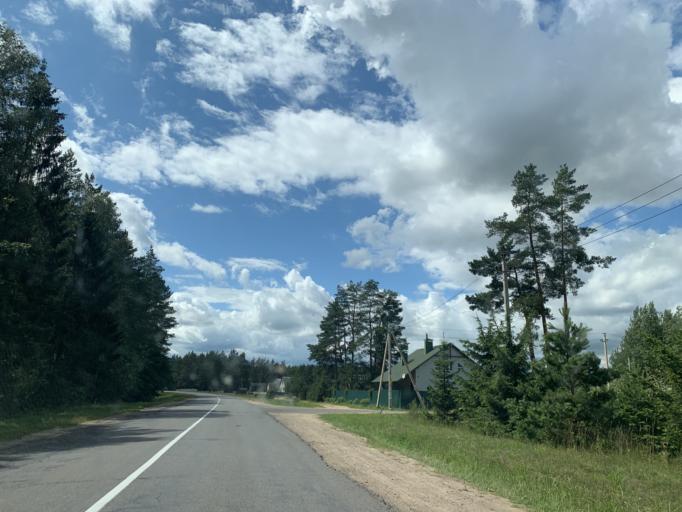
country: BY
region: Minsk
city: Rakaw
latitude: 53.9865
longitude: 26.9481
